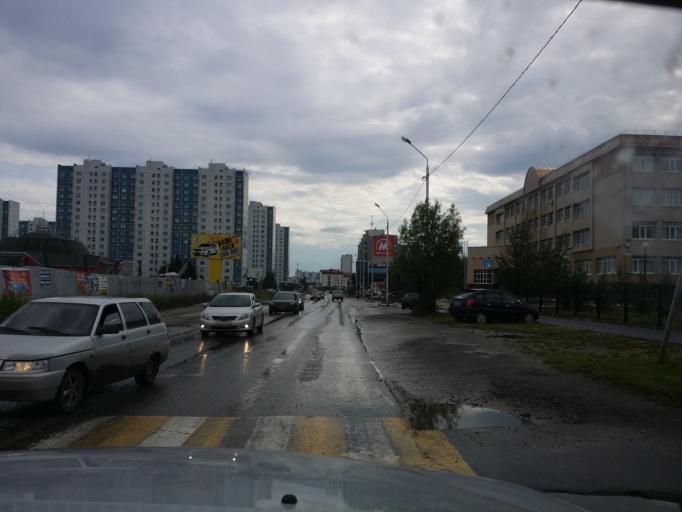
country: RU
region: Khanty-Mansiyskiy Avtonomnyy Okrug
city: Nizhnevartovsk
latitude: 60.9420
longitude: 76.5916
